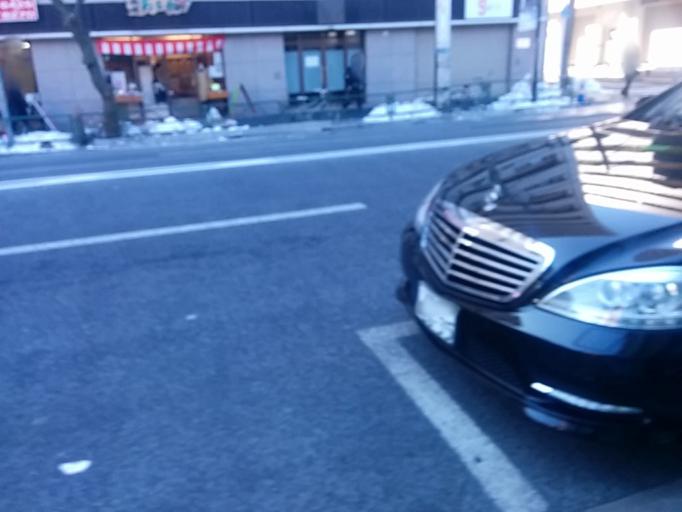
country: JP
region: Tokyo
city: Tokyo
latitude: 35.7327
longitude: 139.7576
